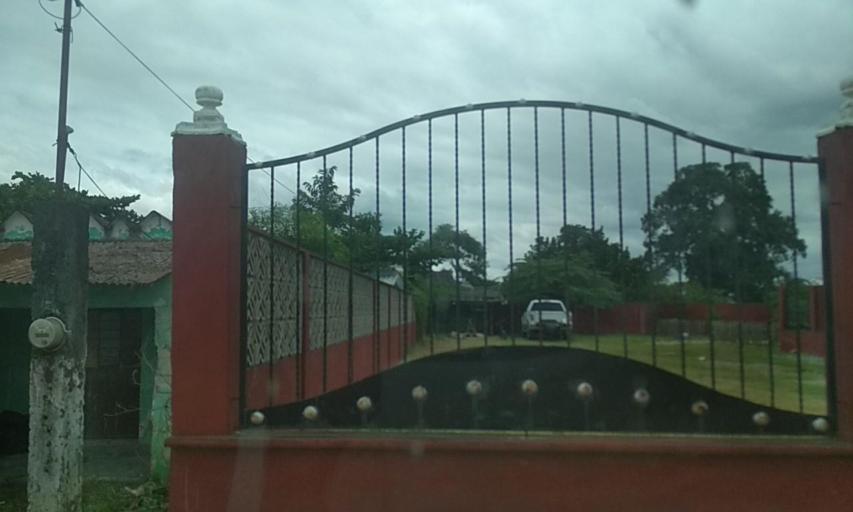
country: MX
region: Veracruz
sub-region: Martinez de la Torre
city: El Progreso
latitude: 20.0950
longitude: -97.0131
